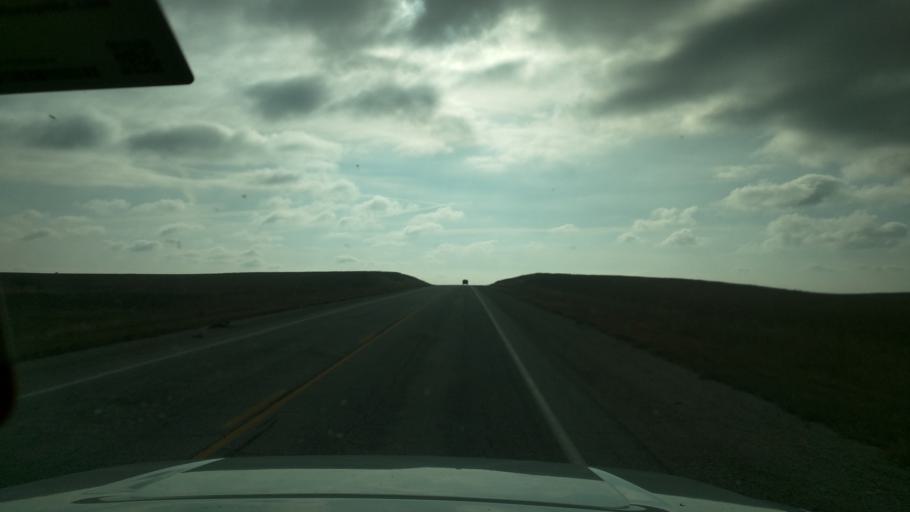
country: US
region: Kansas
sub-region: Chautauqua County
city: Sedan
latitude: 37.0968
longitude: -96.2316
